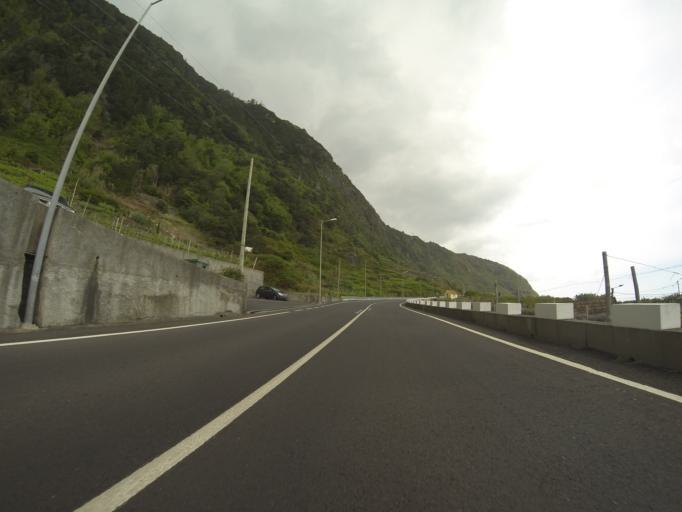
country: PT
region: Madeira
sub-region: Porto Moniz
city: Porto Moniz
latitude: 32.8446
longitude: -17.1454
